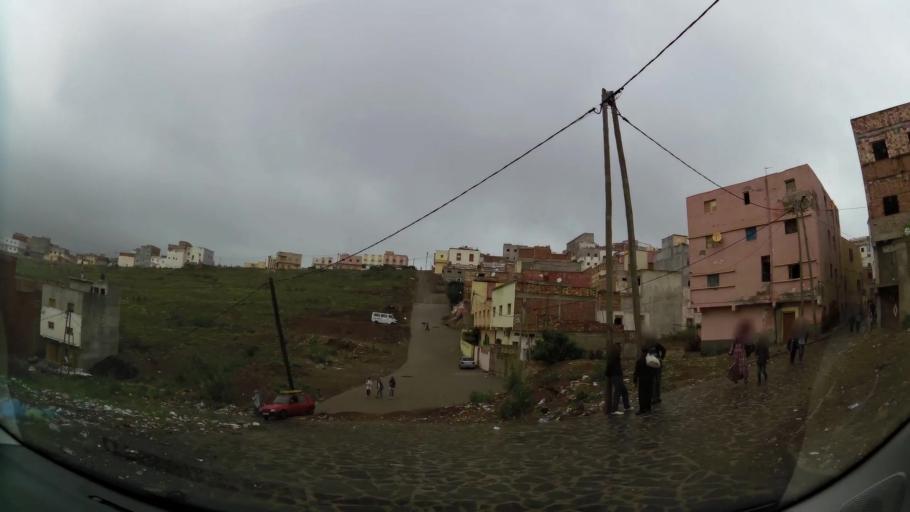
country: MA
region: Oriental
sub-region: Nador
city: Nador
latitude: 35.1812
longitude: -2.9365
